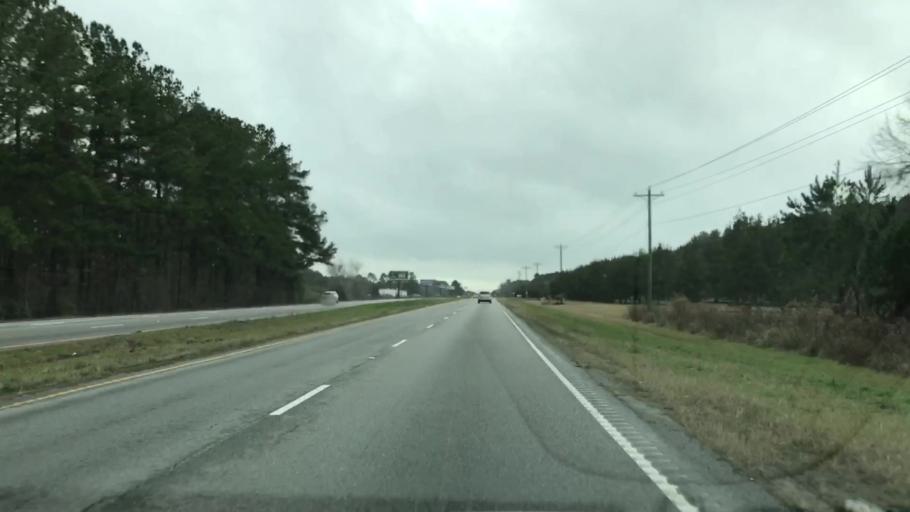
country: US
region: South Carolina
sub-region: Berkeley County
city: Goose Creek
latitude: 33.0421
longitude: -80.0333
